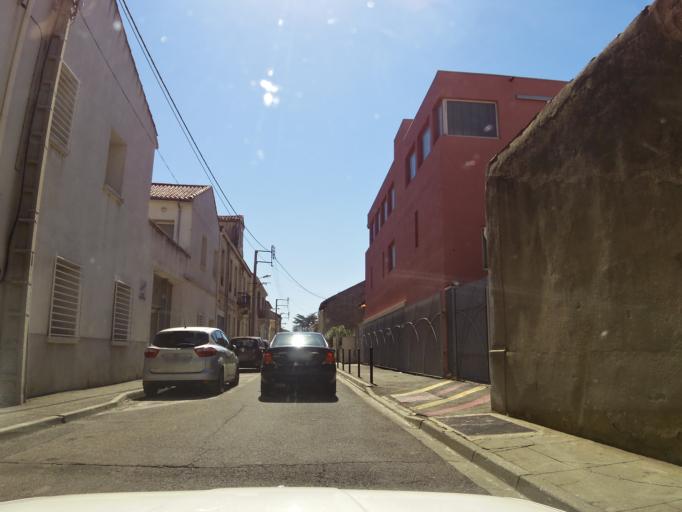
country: FR
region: Languedoc-Roussillon
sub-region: Departement du Gard
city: Nimes
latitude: 43.8336
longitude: 4.3711
